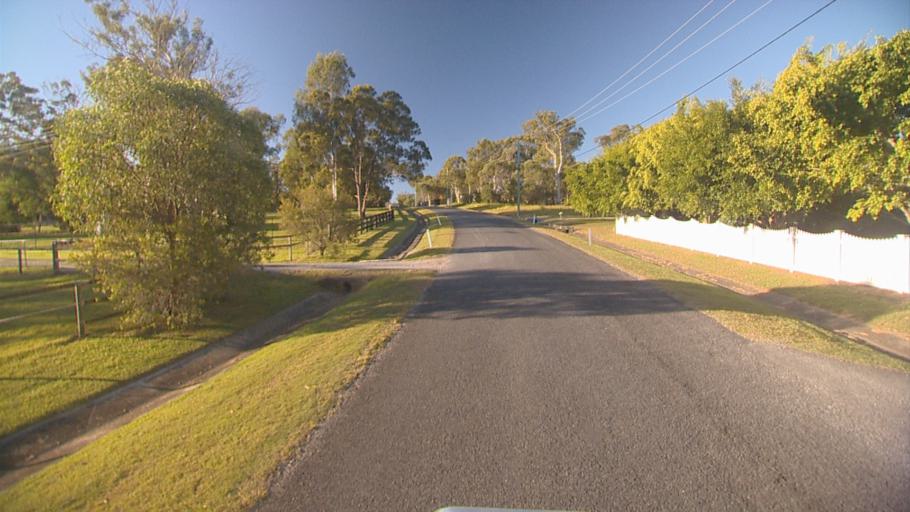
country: AU
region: Queensland
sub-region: Redland
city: Redland Bay
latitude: -27.6630
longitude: 153.2716
